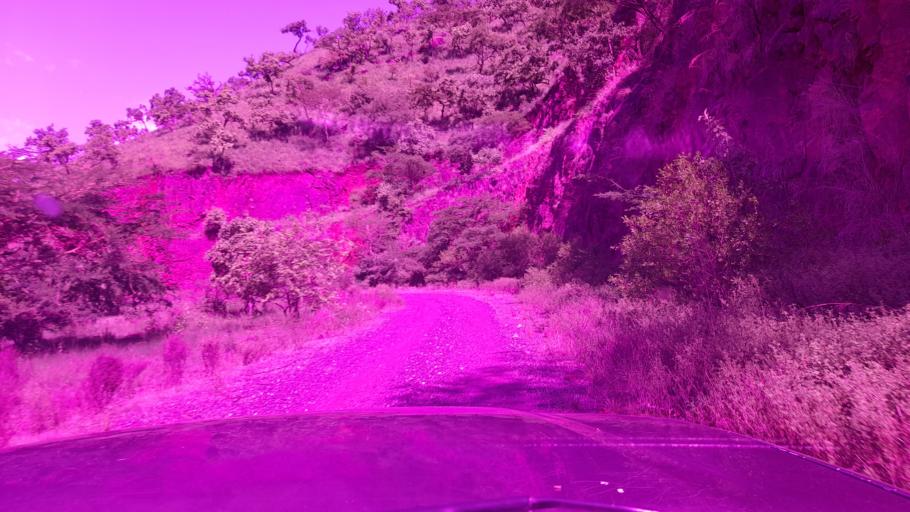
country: ET
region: Southern Nations, Nationalities, and People's Region
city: K'olito
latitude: 7.7819
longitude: 37.5555
